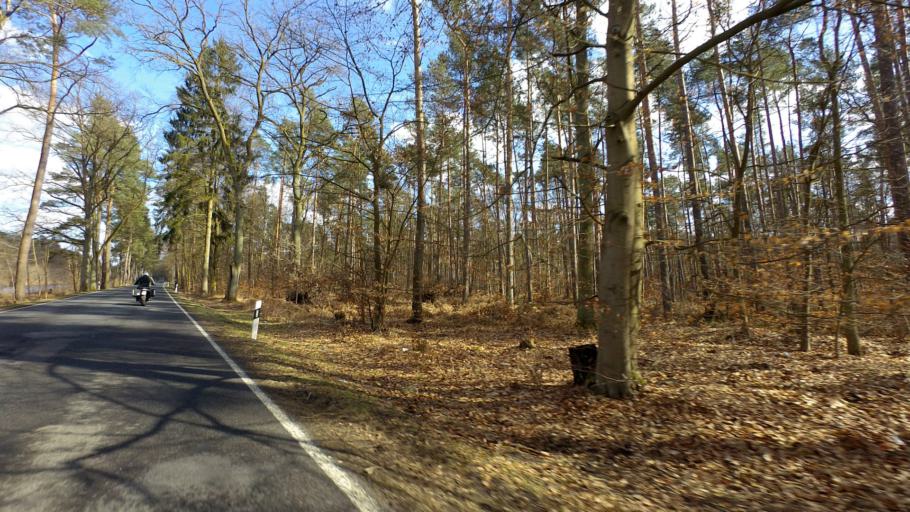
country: DE
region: Brandenburg
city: Marienwerder
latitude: 52.8462
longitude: 13.5259
